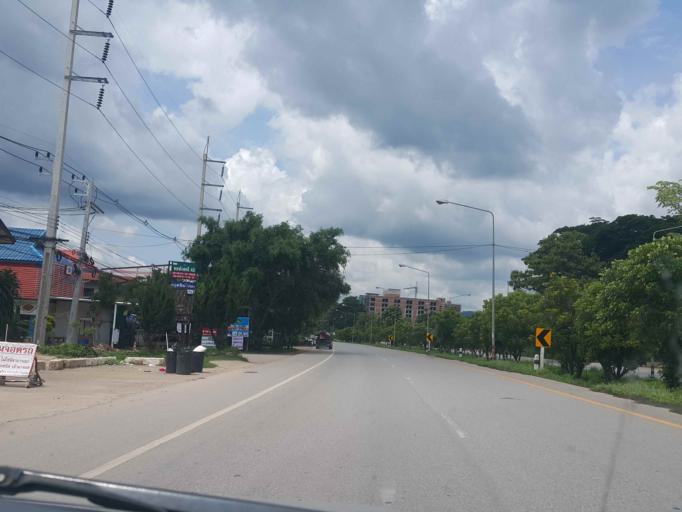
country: TH
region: Phayao
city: Dok Kham Tai
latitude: 19.0261
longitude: 99.9231
